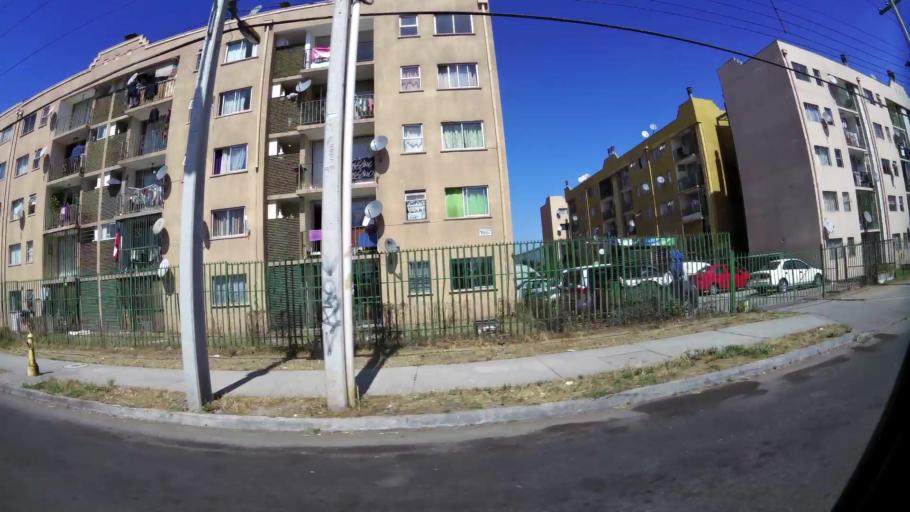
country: CL
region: Santiago Metropolitan
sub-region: Provincia de Santiago
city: Lo Prado
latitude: -33.4854
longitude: -70.7347
